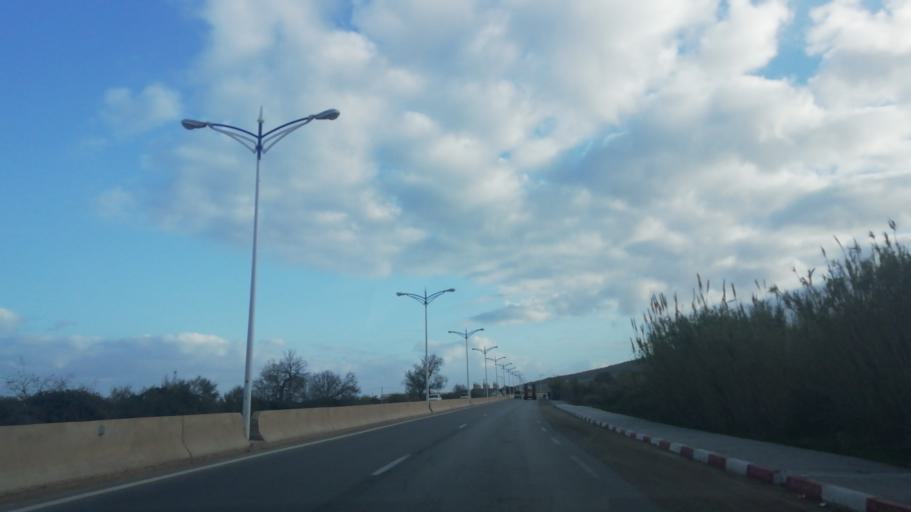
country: DZ
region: Mostaganem
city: Mostaganem
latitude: 36.0244
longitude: 0.1334
